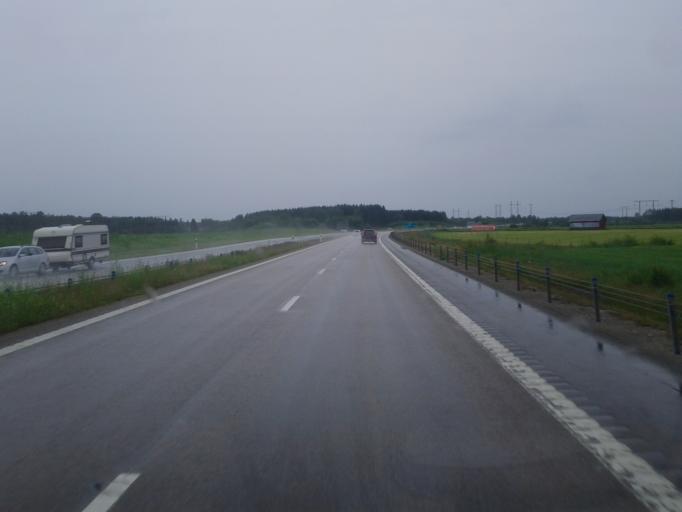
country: SE
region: Uppsala
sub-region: Tierps Kommun
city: Tierp
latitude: 60.3476
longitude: 17.4764
